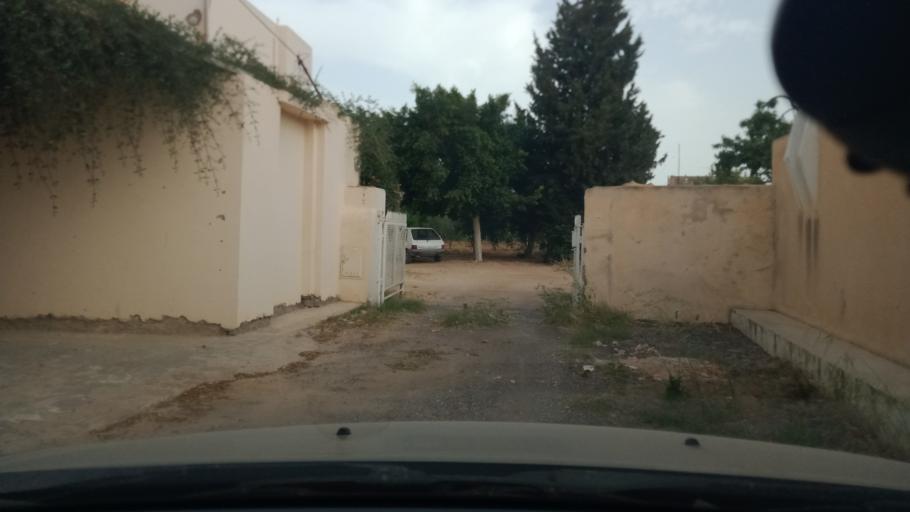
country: TN
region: Safaqis
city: Al Qarmadah
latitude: 34.7847
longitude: 10.7633
